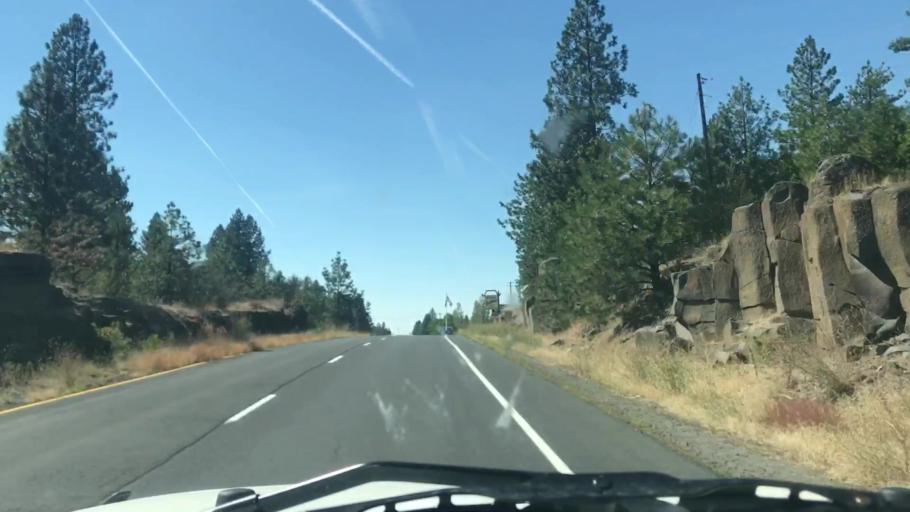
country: US
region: Washington
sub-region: Spokane County
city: Spokane
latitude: 47.6430
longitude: -117.4862
